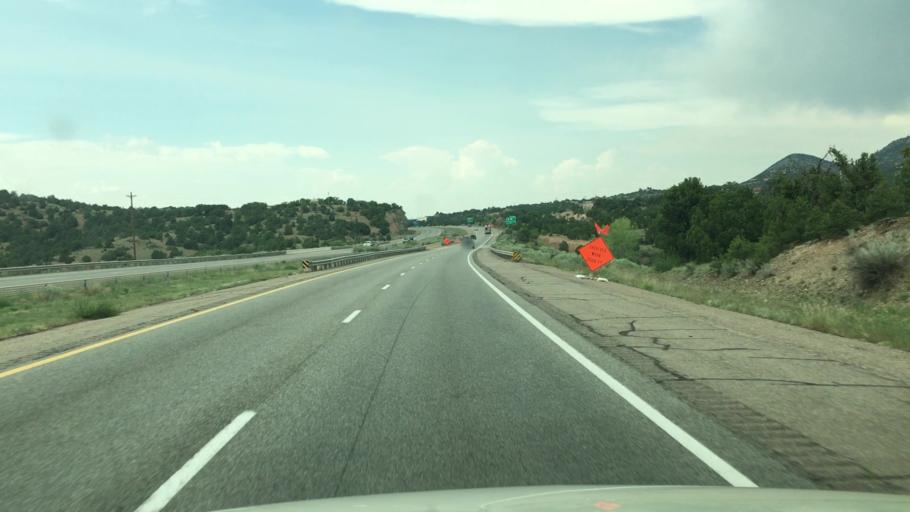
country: US
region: New Mexico
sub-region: Santa Fe County
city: Santa Fe
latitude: 35.6182
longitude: -105.9188
